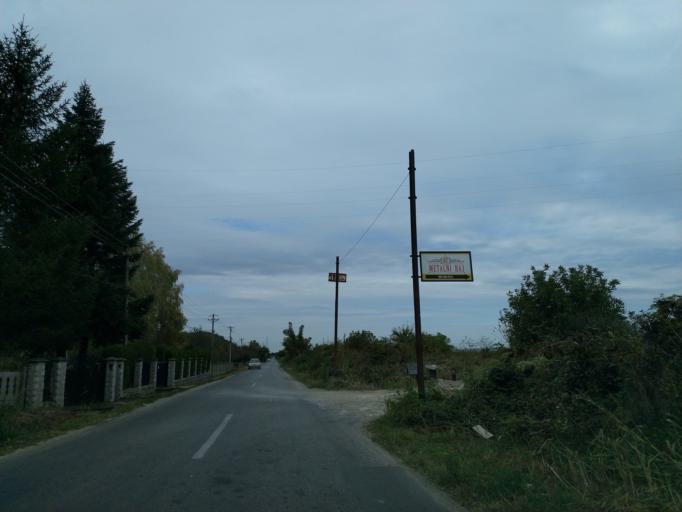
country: RS
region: Central Serbia
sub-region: Pomoravski Okrug
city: Cuprija
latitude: 43.9395
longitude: 21.3205
